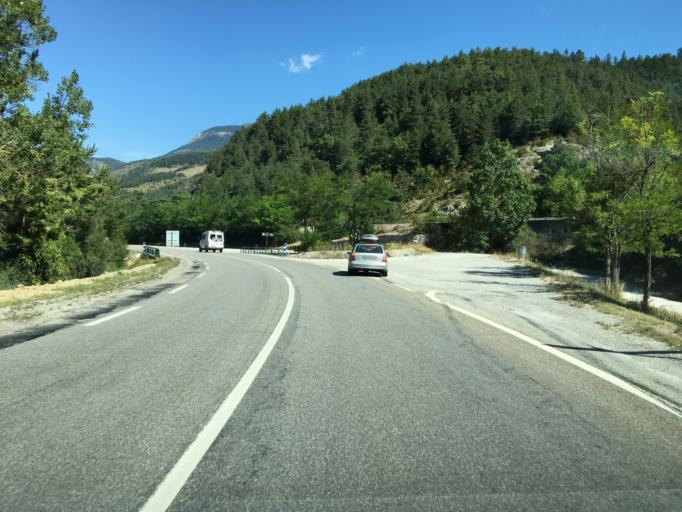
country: FR
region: Provence-Alpes-Cote d'Azur
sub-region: Departement des Hautes-Alpes
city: Veynes
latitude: 44.5554
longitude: 5.7673
